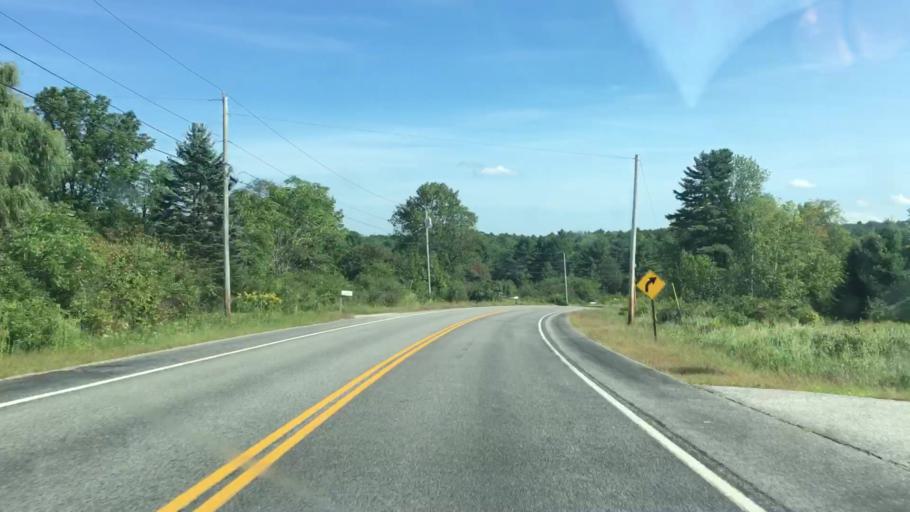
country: US
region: Maine
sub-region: Androscoggin County
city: Lisbon
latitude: 44.0506
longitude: -70.0801
